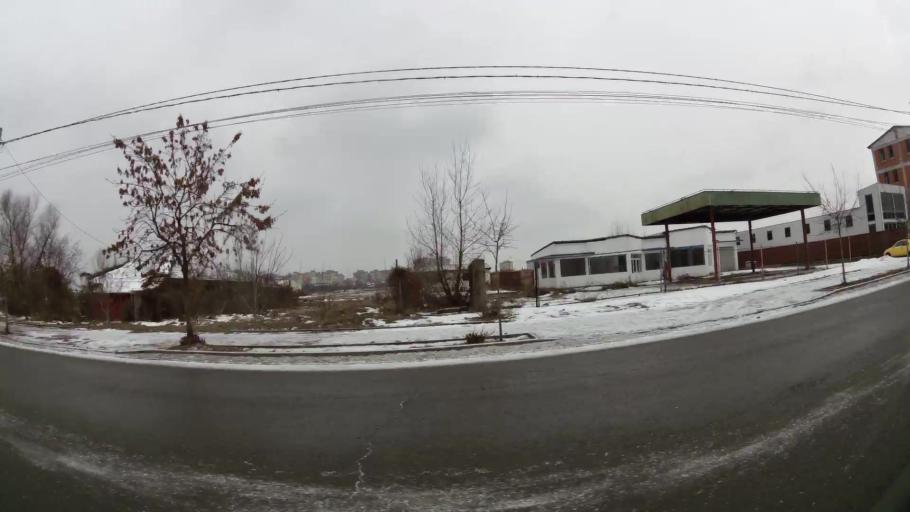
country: RO
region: Dambovita
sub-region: Municipiul Targoviste
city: Targoviste
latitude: 44.9251
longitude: 25.4844
